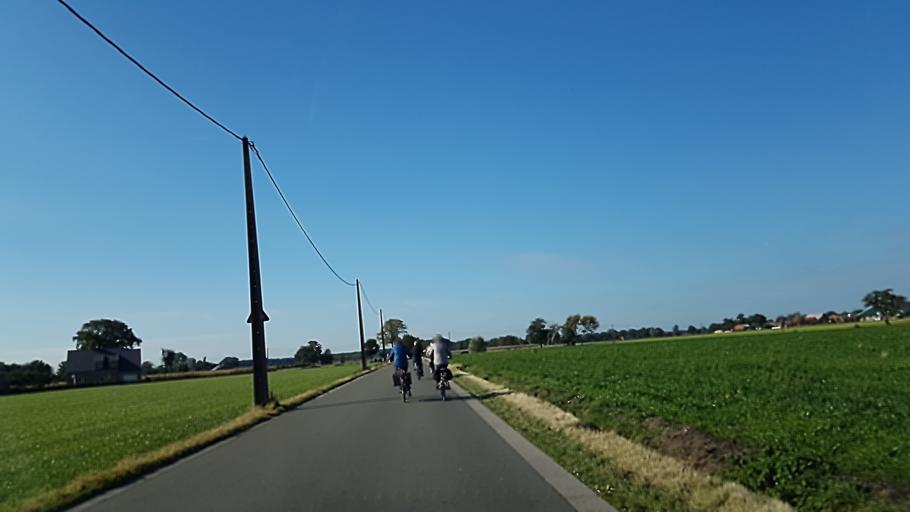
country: BE
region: Flanders
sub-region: Provincie Antwerpen
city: Essen
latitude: 51.4321
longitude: 4.4142
